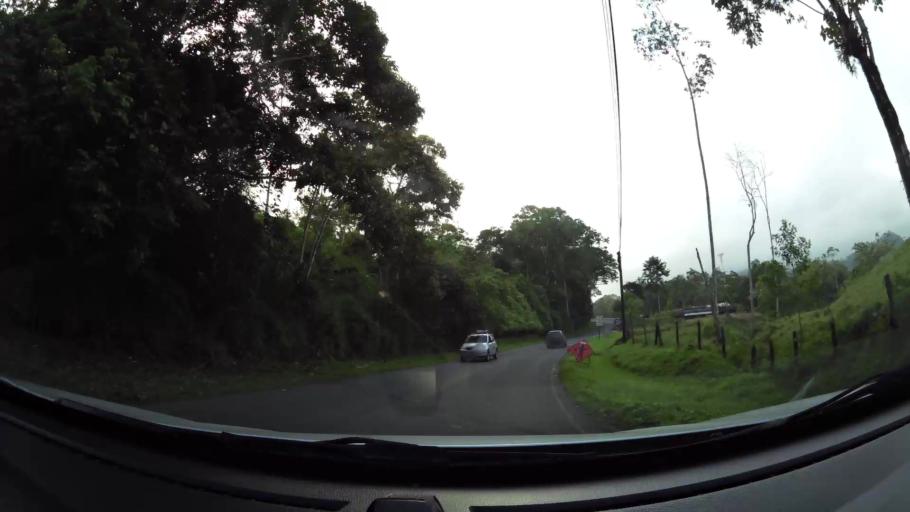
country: CR
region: Cartago
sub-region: Canton de Turrialba
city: La Suiza
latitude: 9.9647
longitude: -83.5696
